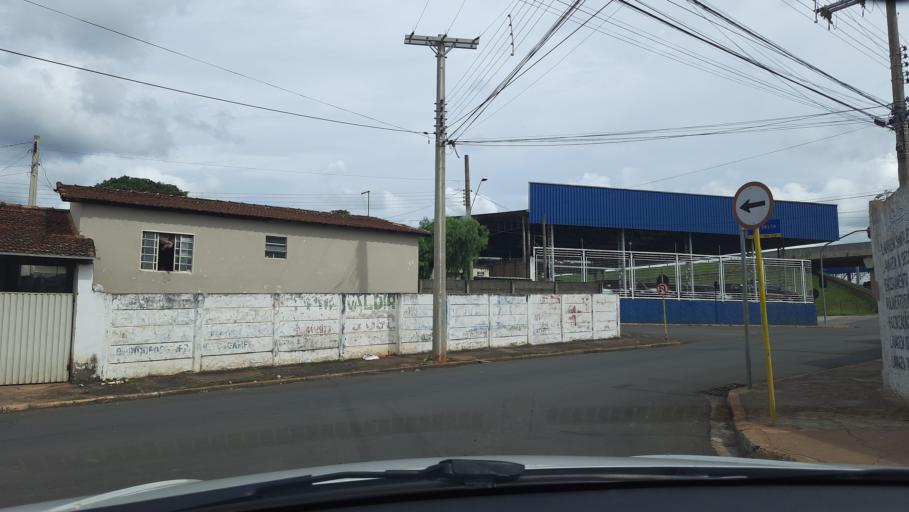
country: BR
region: Sao Paulo
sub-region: Vargem Grande Do Sul
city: Vargem Grande do Sul
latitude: -21.8436
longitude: -46.8981
